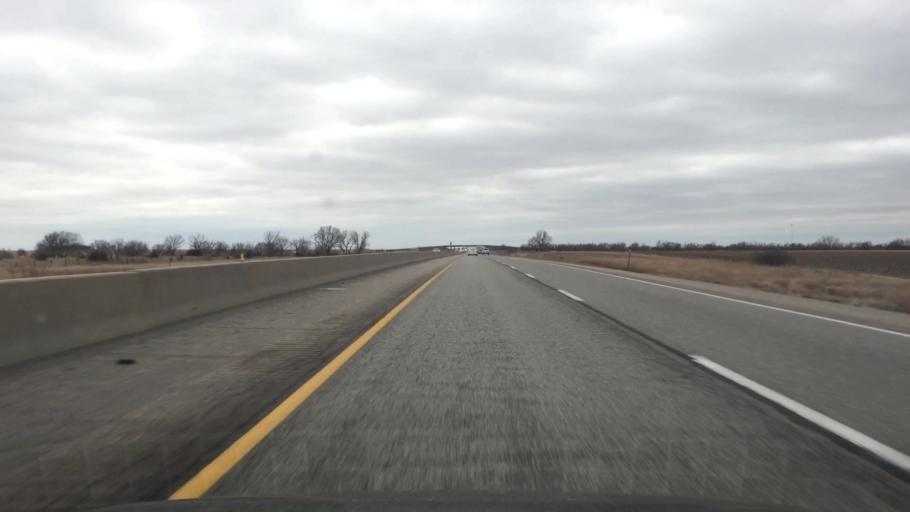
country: US
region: Kansas
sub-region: Butler County
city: El Dorado
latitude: 38.0210
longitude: -96.6682
